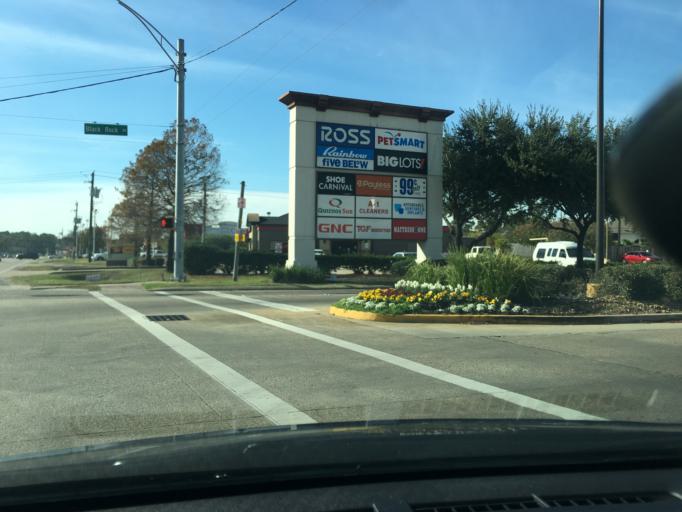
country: US
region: Texas
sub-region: Harris County
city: Cloverleaf
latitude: 29.8080
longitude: -95.1664
